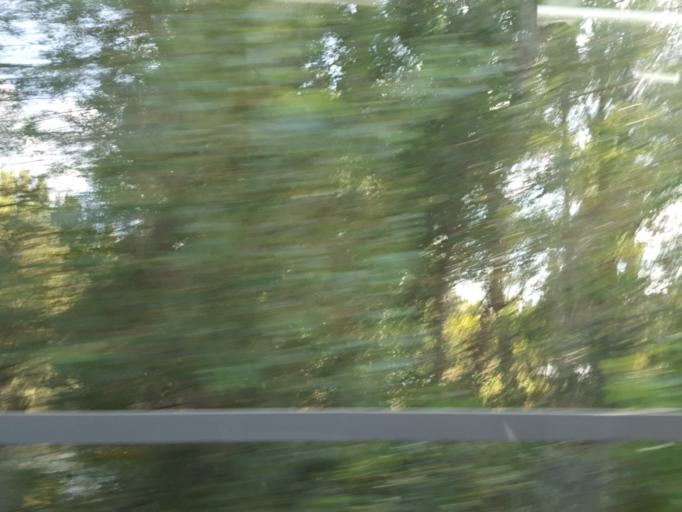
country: TR
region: Tokat
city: Sulusaray
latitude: 39.9767
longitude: 36.0561
